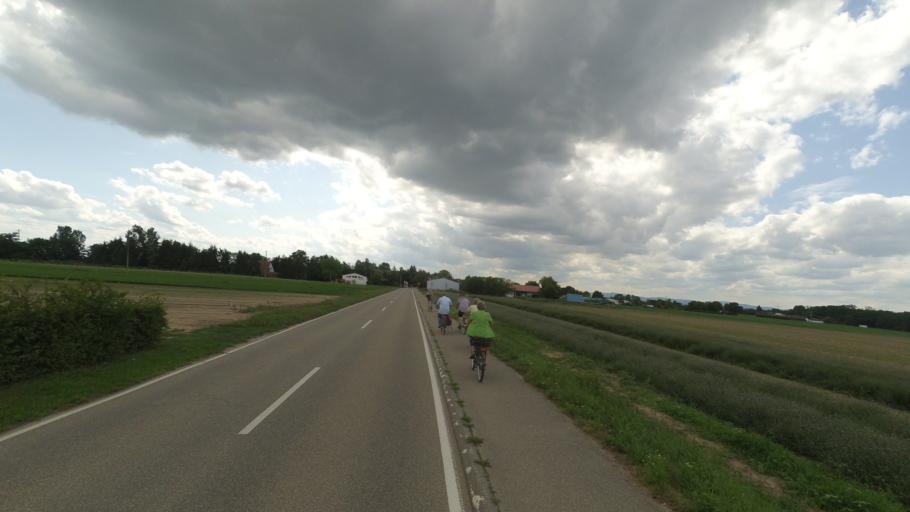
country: DE
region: Rheinland-Pfalz
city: Limburgerhof
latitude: 49.4072
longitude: 8.4019
